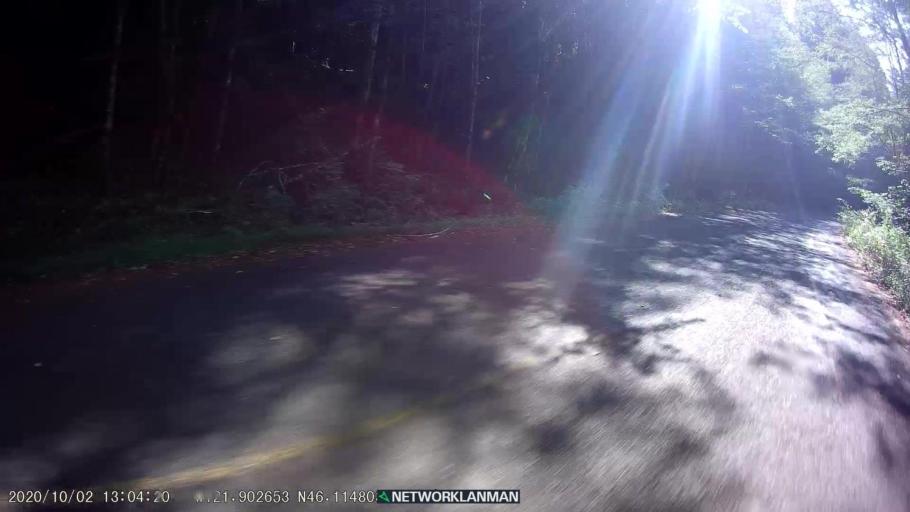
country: US
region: Washington
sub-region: Skamania County
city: Carson
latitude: 46.1145
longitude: -121.9027
